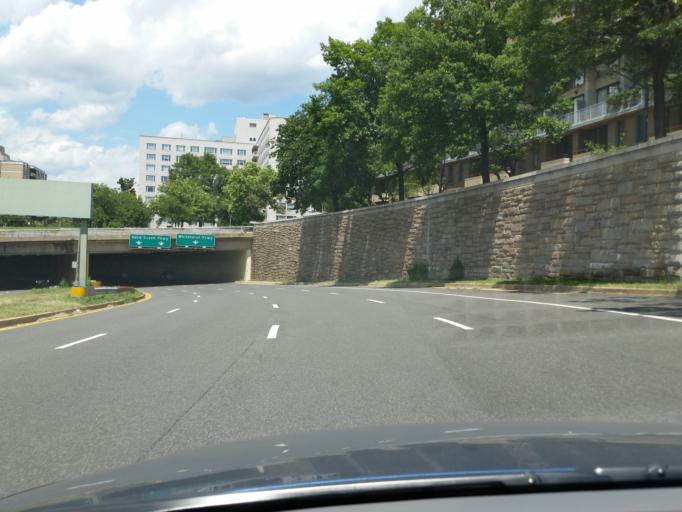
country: US
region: Washington, D.C.
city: Washington, D.C.
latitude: 38.8972
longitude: -77.0528
